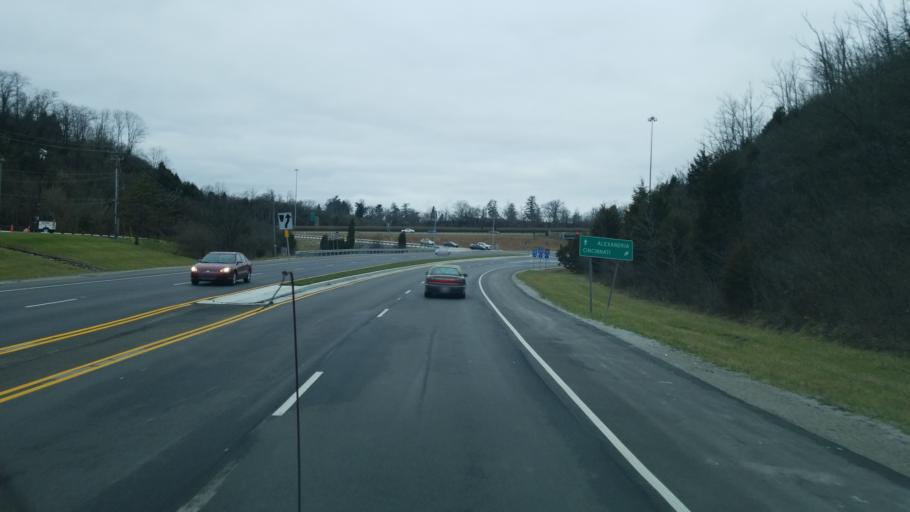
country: US
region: Kentucky
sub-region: Campbell County
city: Southgate
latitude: 39.0643
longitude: -84.4624
